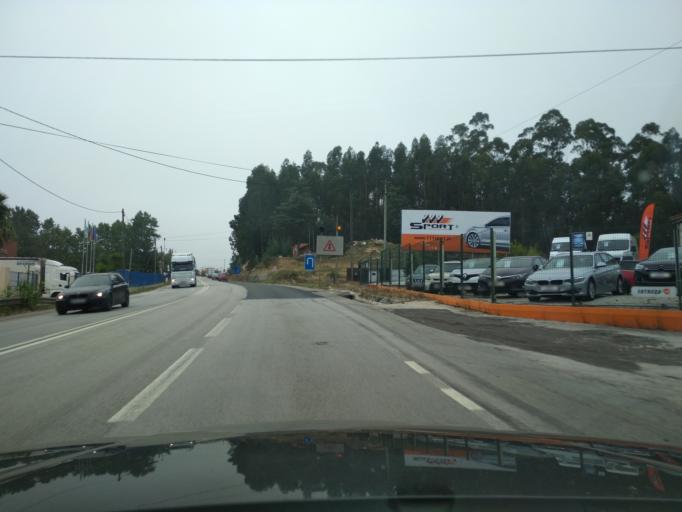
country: PT
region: Aveiro
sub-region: Mealhada
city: Pampilhosa do Botao
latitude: 40.3017
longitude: -8.4471
